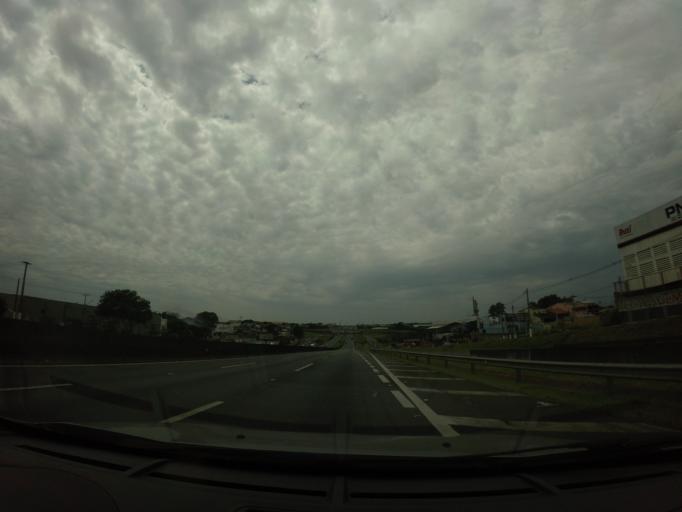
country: BR
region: Sao Paulo
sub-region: Hortolandia
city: Hortolandia
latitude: -22.8178
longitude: -47.2023
